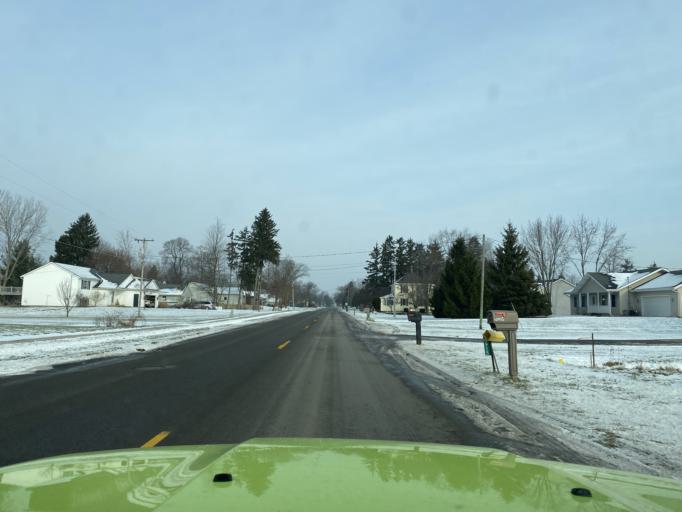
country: US
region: Michigan
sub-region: Ottawa County
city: Allendale
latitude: 42.9672
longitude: -85.9242
